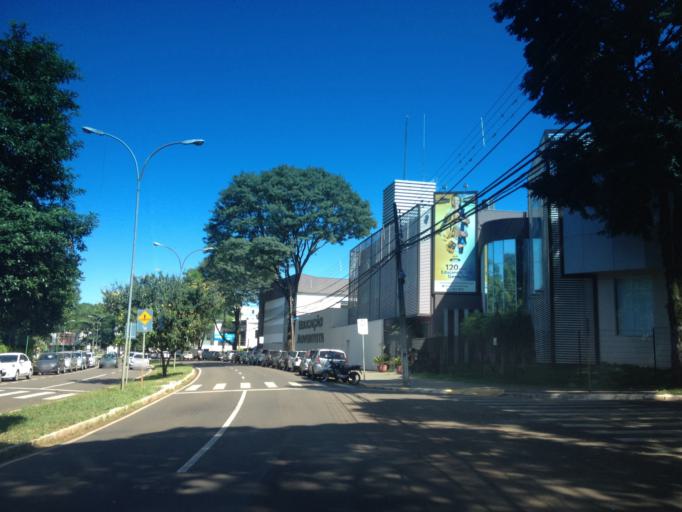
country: BR
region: Parana
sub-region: Maringa
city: Maringa
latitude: -23.4269
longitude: -51.9470
